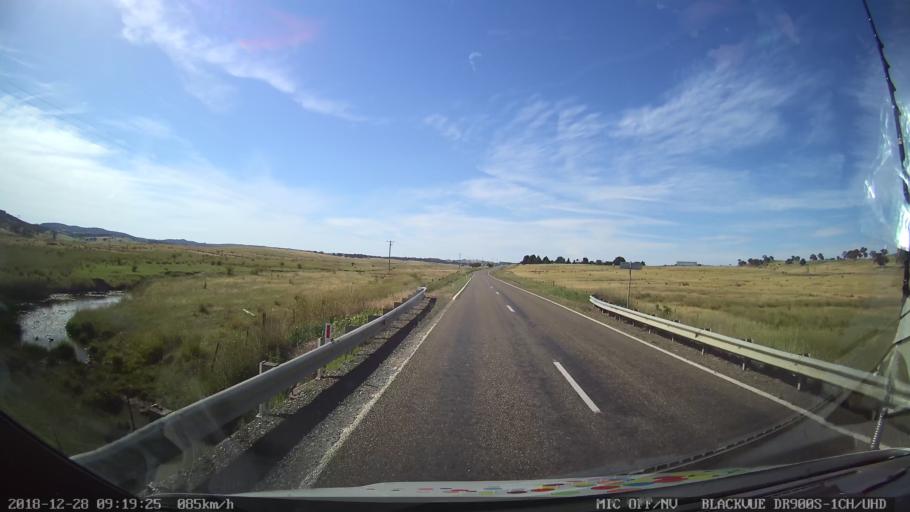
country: AU
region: New South Wales
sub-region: Upper Lachlan Shire
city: Crookwell
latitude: -34.3363
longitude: 149.3686
